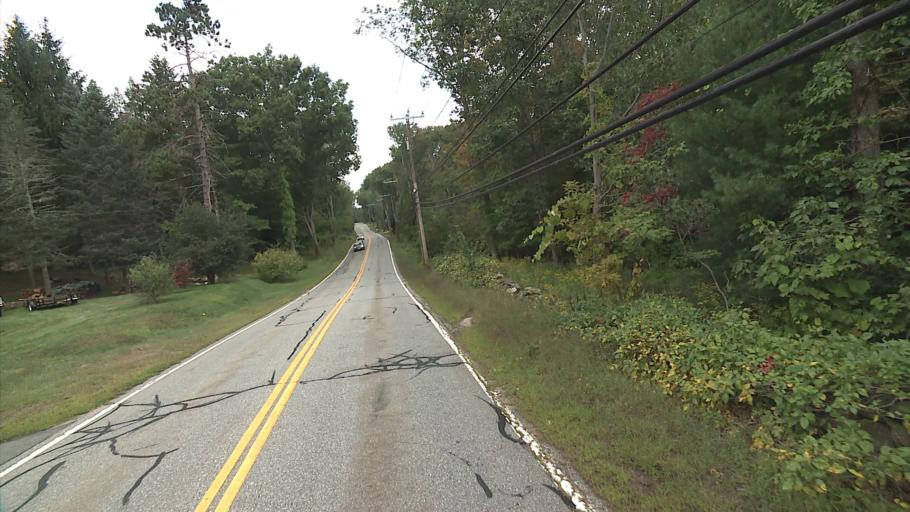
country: US
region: Connecticut
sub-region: Tolland County
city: Storrs
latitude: 41.8482
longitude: -72.2732
